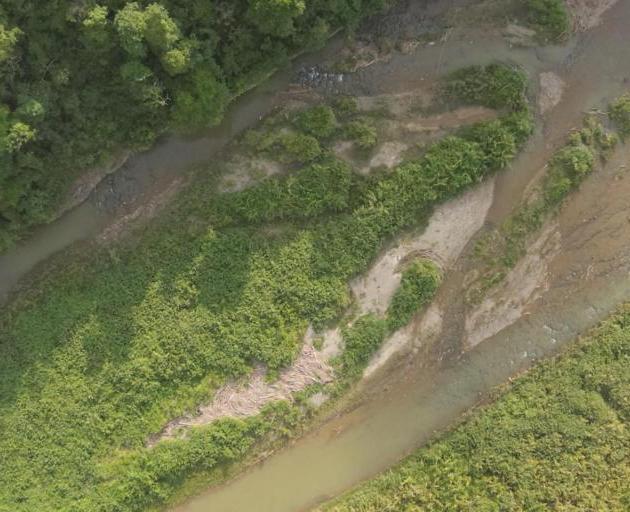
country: BO
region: La Paz
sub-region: Provincia Larecaja
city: Guanay
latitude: -15.7728
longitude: -67.6616
